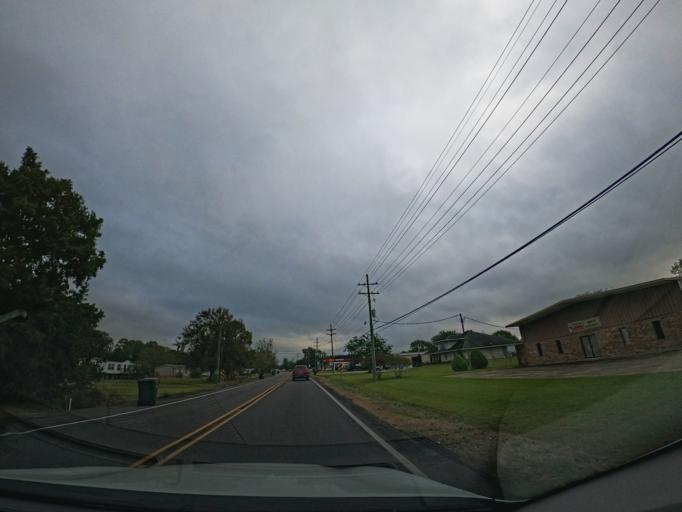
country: US
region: Louisiana
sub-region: Terrebonne Parish
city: Presquille
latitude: 29.5036
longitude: -90.6766
